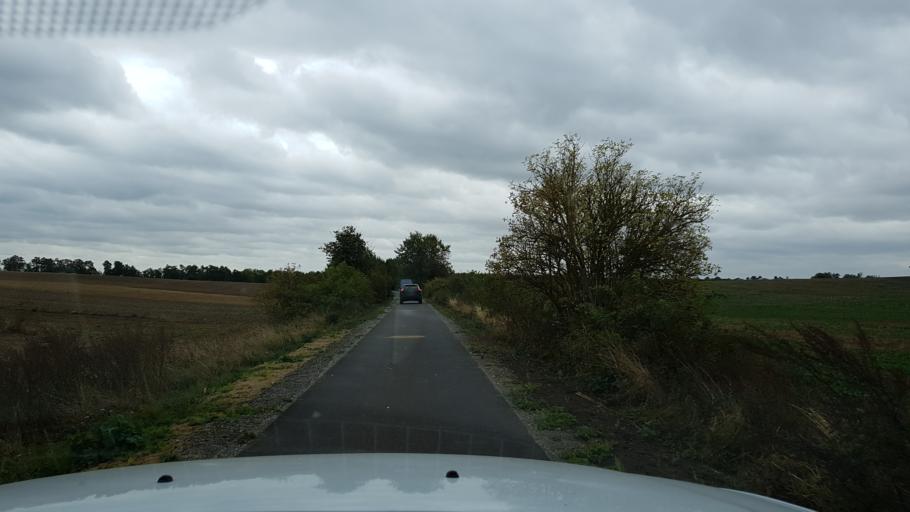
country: PL
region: West Pomeranian Voivodeship
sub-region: Powiat gryfinski
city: Cedynia
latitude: 52.8558
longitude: 14.2827
